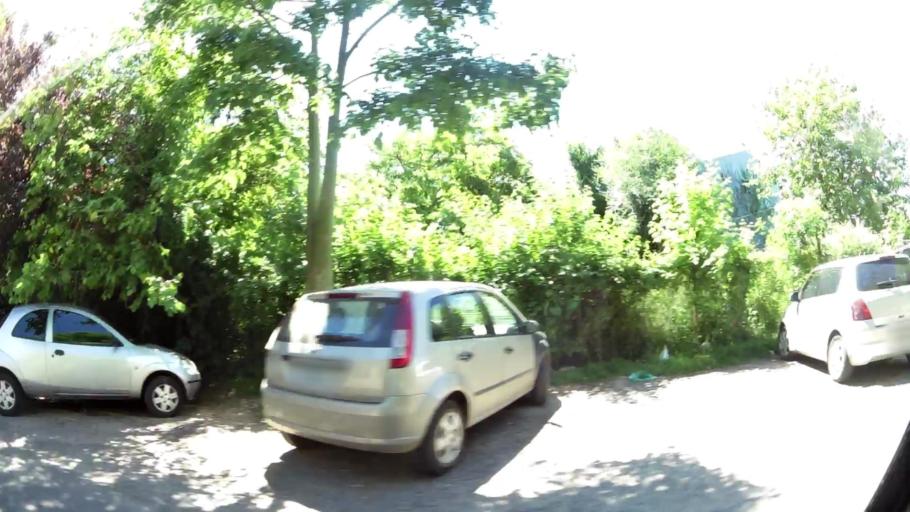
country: AR
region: Buenos Aires
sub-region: Partido de San Isidro
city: San Isidro
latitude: -34.4713
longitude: -58.4949
